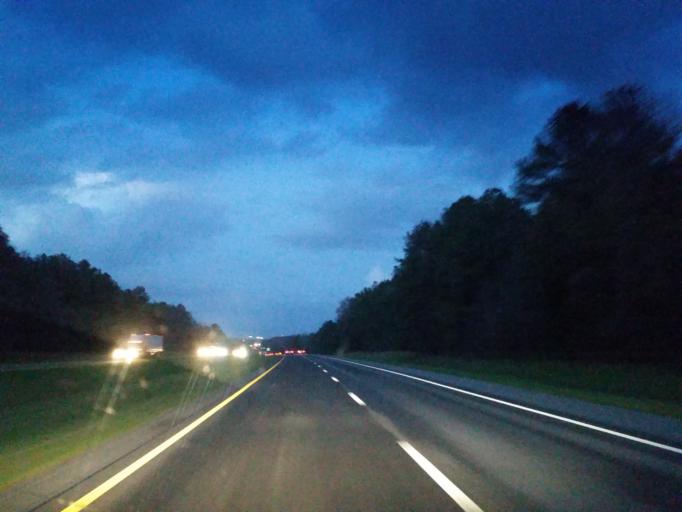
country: US
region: Alabama
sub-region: Sumter County
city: Livingston
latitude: 32.5994
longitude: -88.2217
